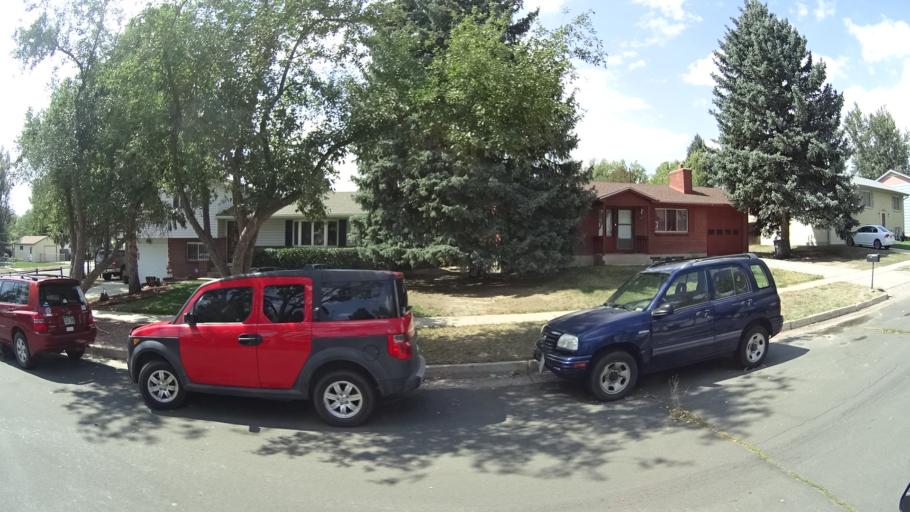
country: US
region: Colorado
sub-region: El Paso County
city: Colorado Springs
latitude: 38.8492
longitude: -104.7686
